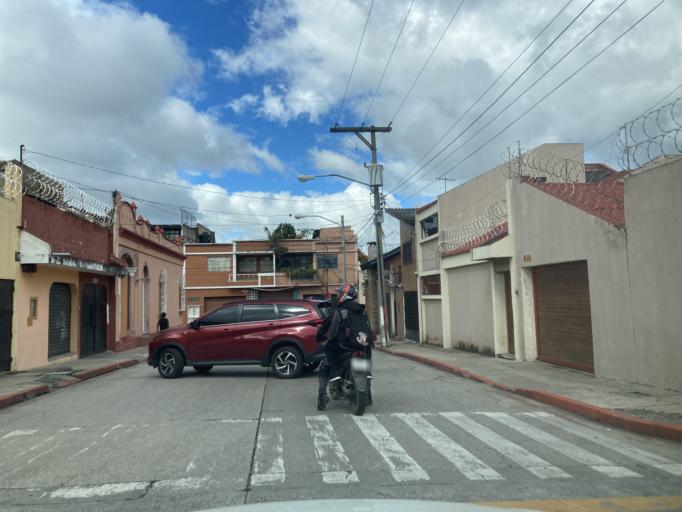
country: GT
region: Guatemala
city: Guatemala City
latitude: 14.6484
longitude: -90.5139
